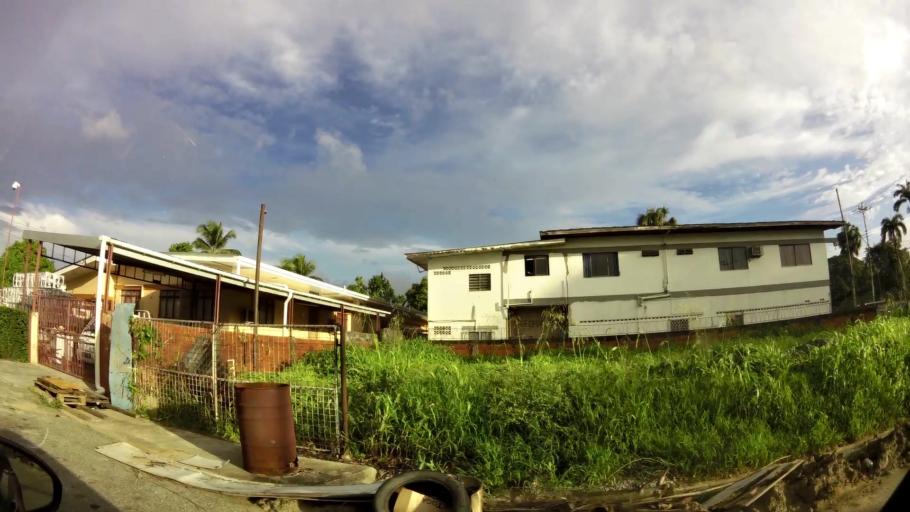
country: TT
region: Tunapuna/Piarco
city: Tunapuna
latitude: 10.6423
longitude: -61.4028
